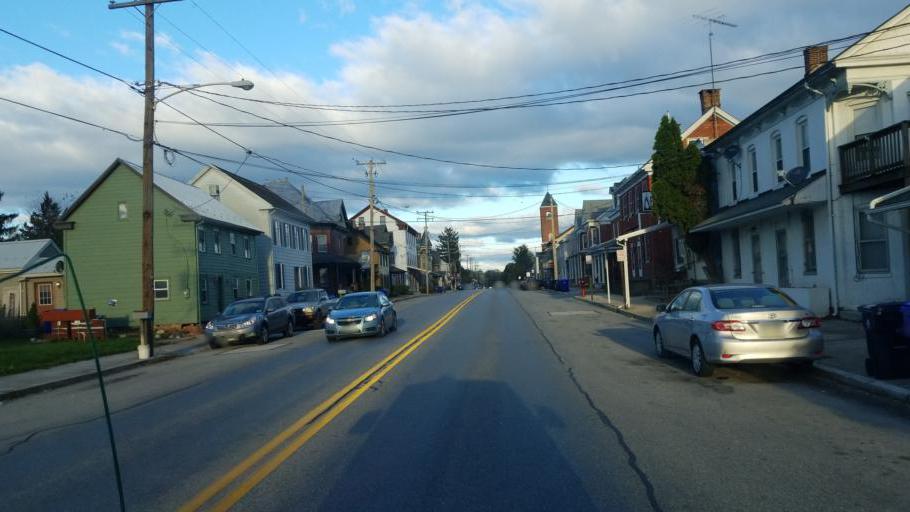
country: US
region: Pennsylvania
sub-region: Adams County
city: East Berlin
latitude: 39.9387
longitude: -76.9815
